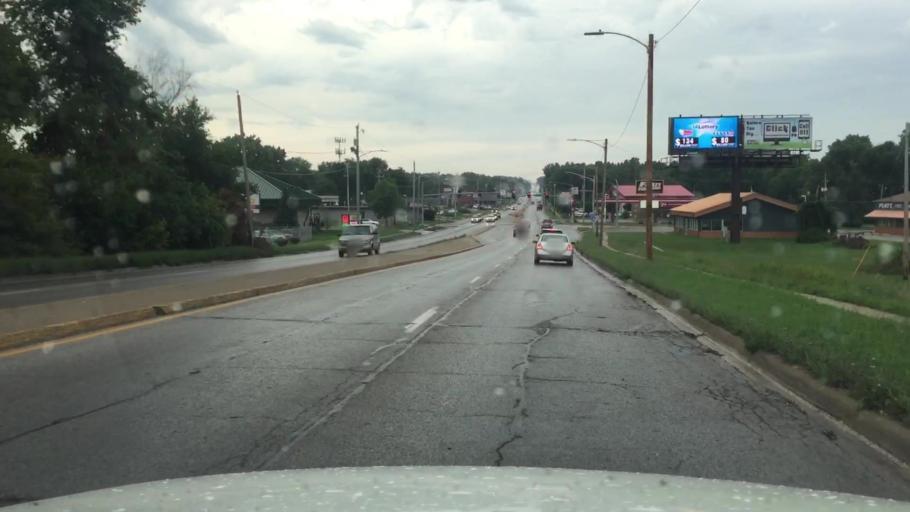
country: US
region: Iowa
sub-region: Polk County
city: Des Moines
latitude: 41.5829
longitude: -93.5970
